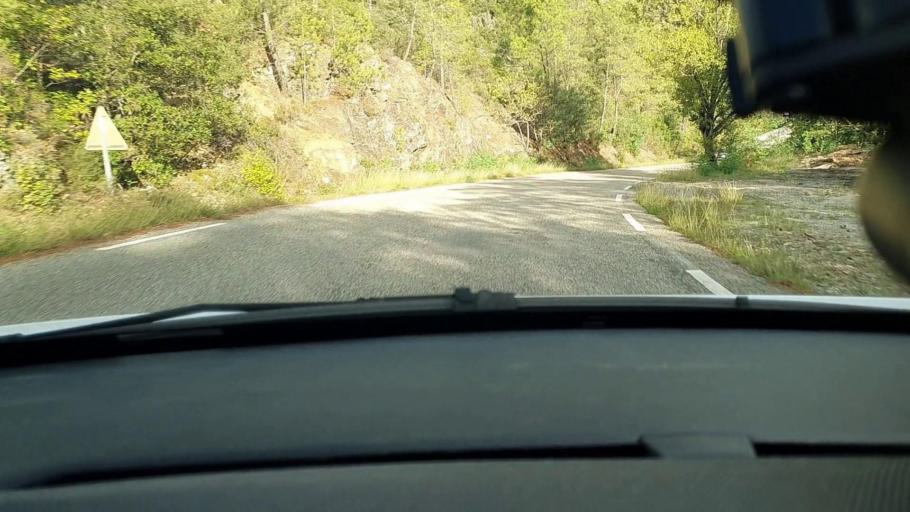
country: FR
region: Languedoc-Roussillon
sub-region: Departement du Gard
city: Besseges
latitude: 44.3178
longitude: 4.0383
